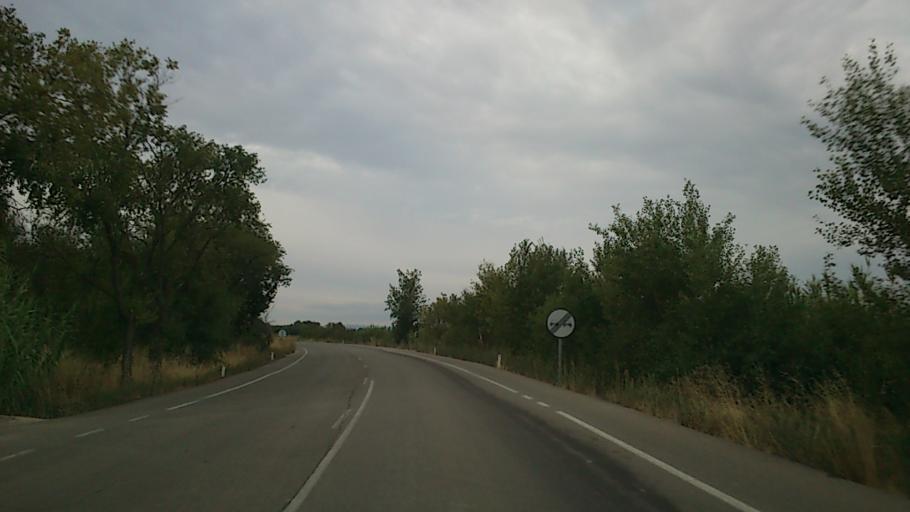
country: ES
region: Aragon
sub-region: Provincia de Zaragoza
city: Villanueva de Gallego
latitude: 41.7799
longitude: -0.7885
